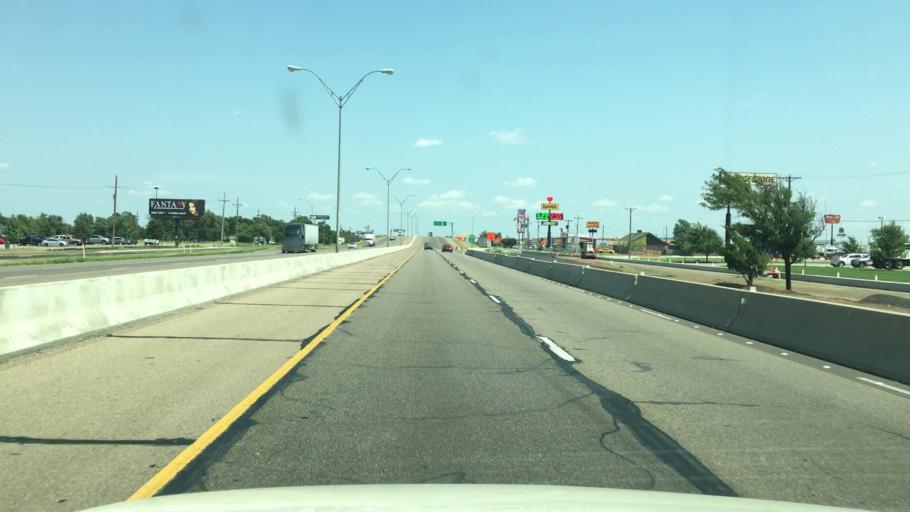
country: US
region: Texas
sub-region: Potter County
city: Amarillo
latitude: 35.1926
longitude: -101.7661
